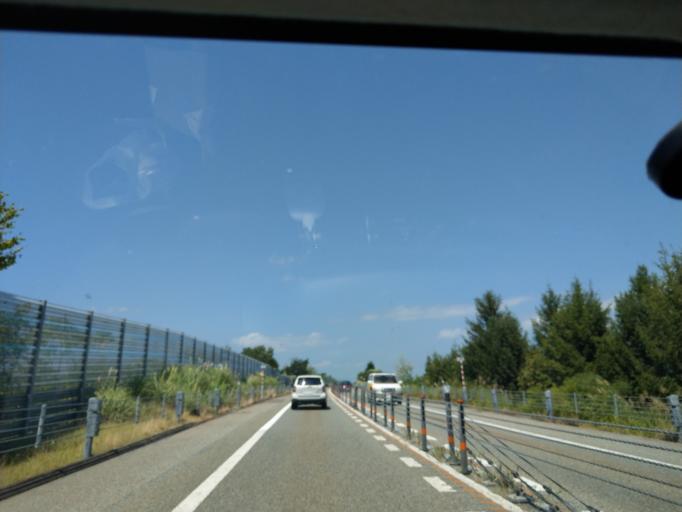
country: JP
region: Akita
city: Omagari
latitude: 39.3800
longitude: 140.4804
